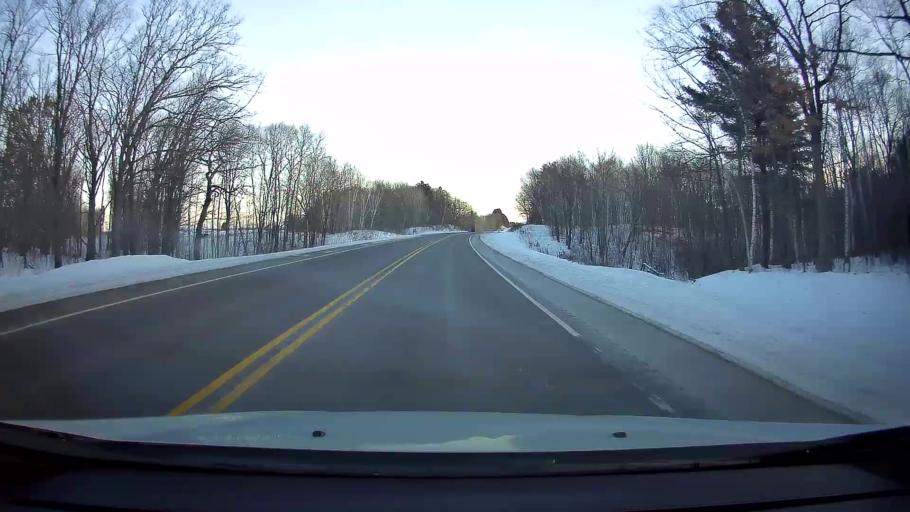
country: US
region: Wisconsin
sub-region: Washburn County
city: Shell Lake
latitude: 45.6760
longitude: -91.9911
